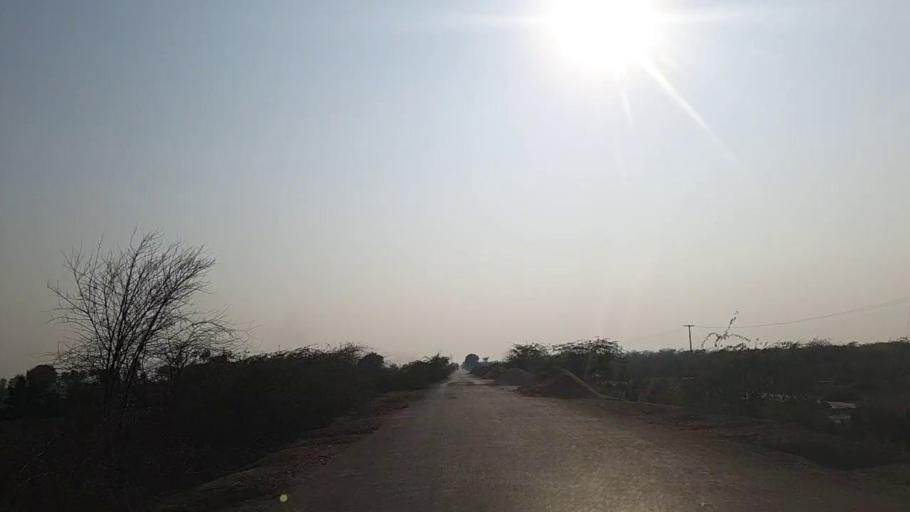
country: PK
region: Sindh
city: Jam Sahib
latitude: 26.2668
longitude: 68.6085
